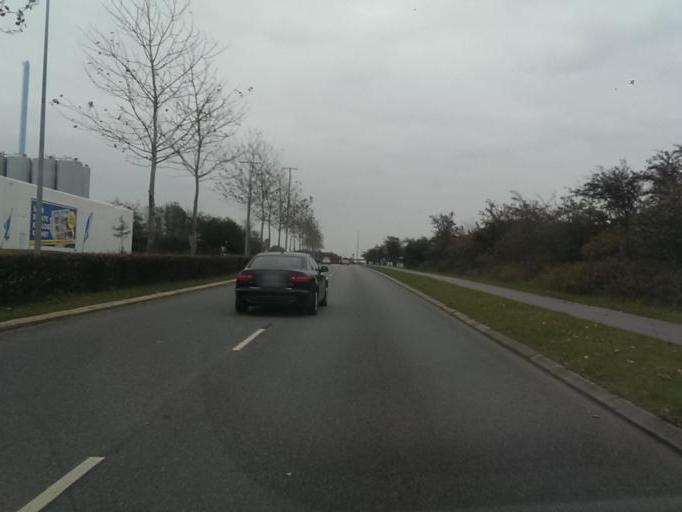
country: DK
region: South Denmark
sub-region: Esbjerg Kommune
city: Esbjerg
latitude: 55.5084
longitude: 8.4627
